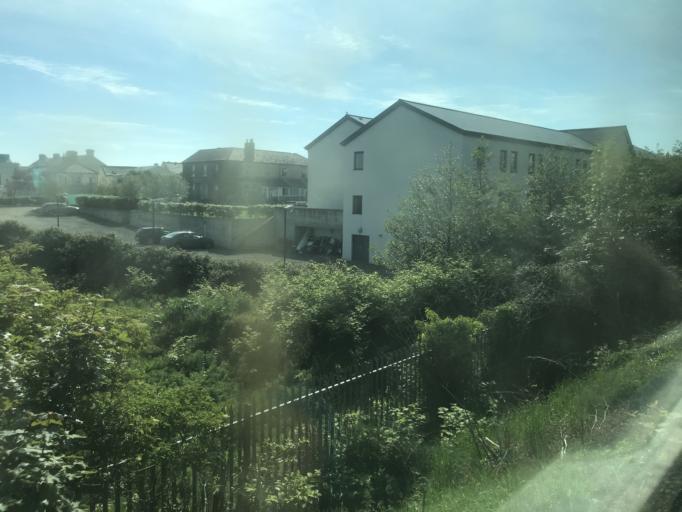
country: IE
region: Leinster
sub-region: Wicklow
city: Greystones
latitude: 53.1491
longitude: -6.0673
